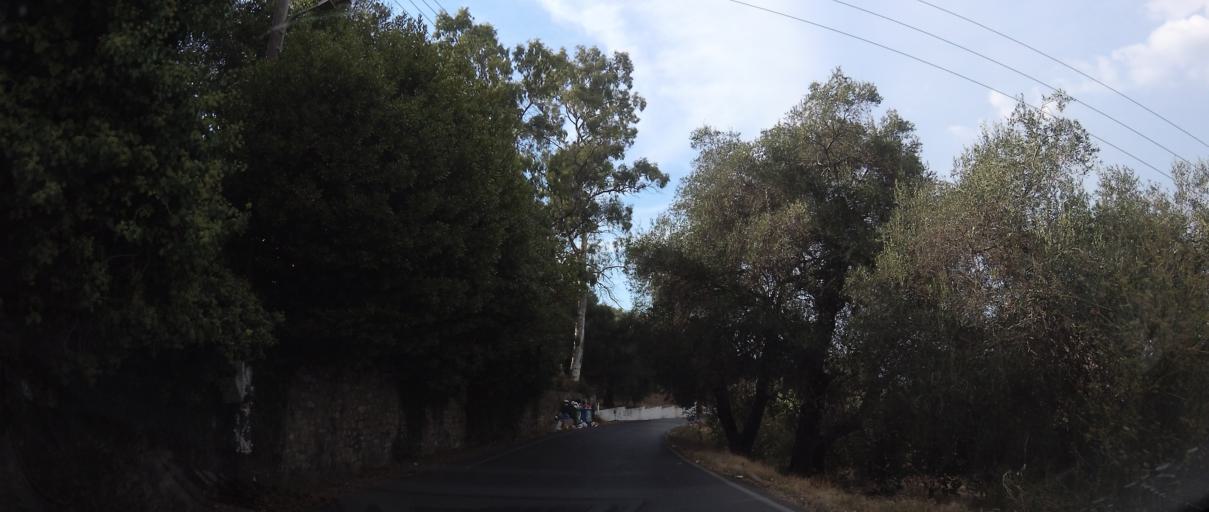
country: GR
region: Ionian Islands
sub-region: Nomos Kerkyras
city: Kynopiastes
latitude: 39.5532
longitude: 19.8624
